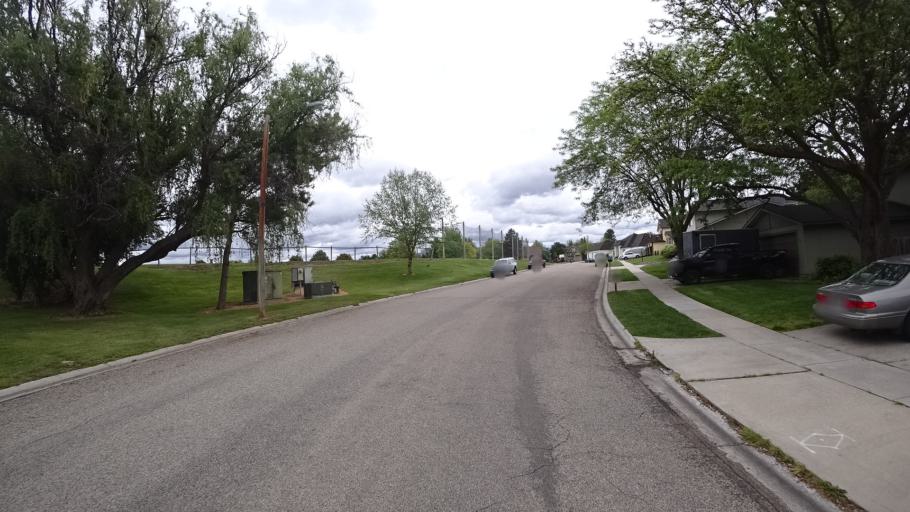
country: US
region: Idaho
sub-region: Ada County
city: Eagle
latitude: 43.6996
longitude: -116.3363
